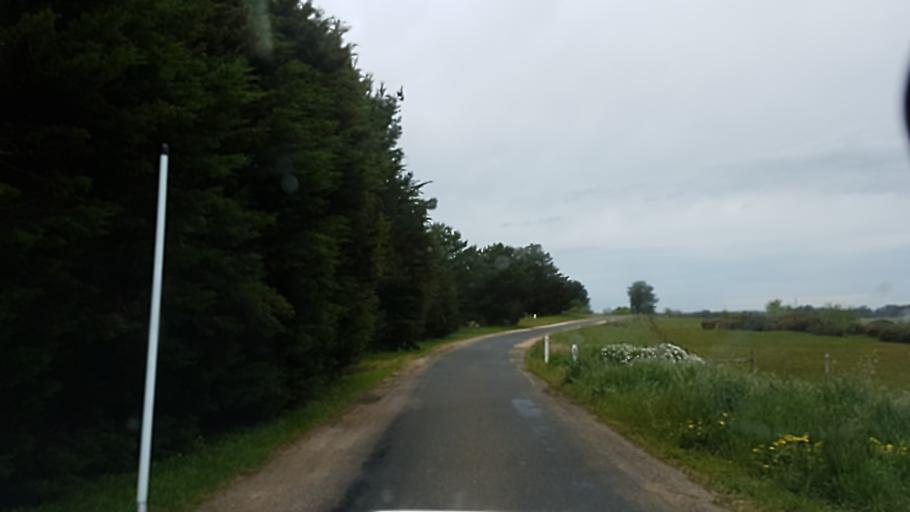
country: AU
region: Victoria
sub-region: Ballarat North
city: Mount Clear
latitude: -37.7791
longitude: 144.0298
